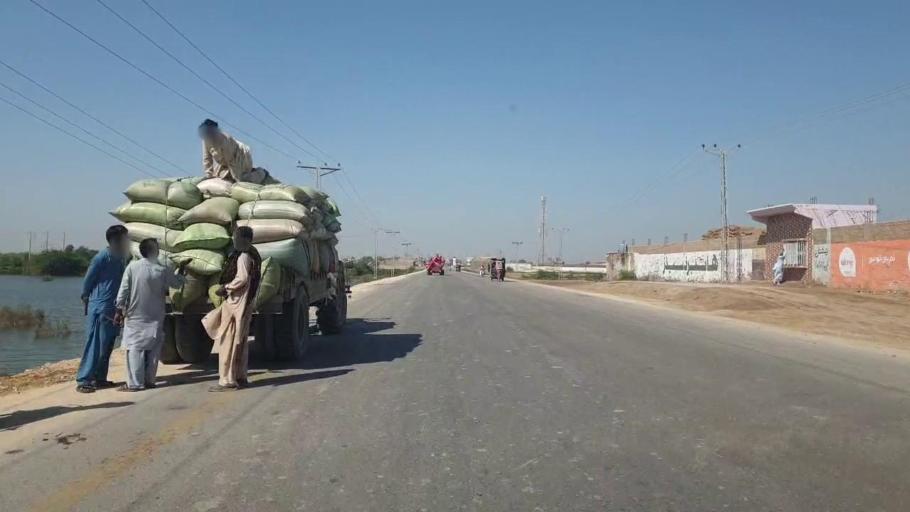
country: PK
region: Sindh
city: Talhar
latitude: 24.8786
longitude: 68.8130
